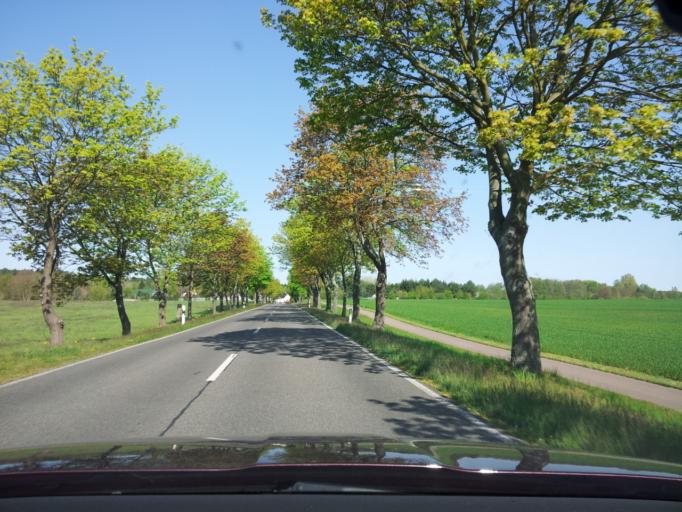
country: DE
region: Brandenburg
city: Juterbog
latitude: 52.0153
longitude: 13.0624
